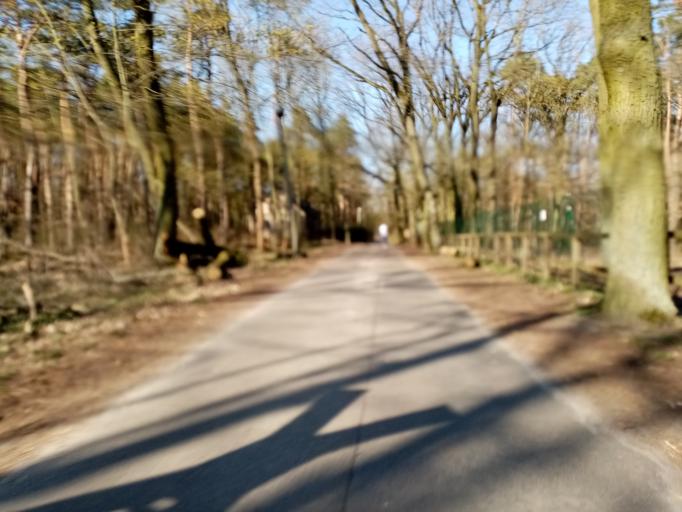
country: DE
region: Berlin
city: Oberschoneweide
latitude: 52.4639
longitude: 13.5408
